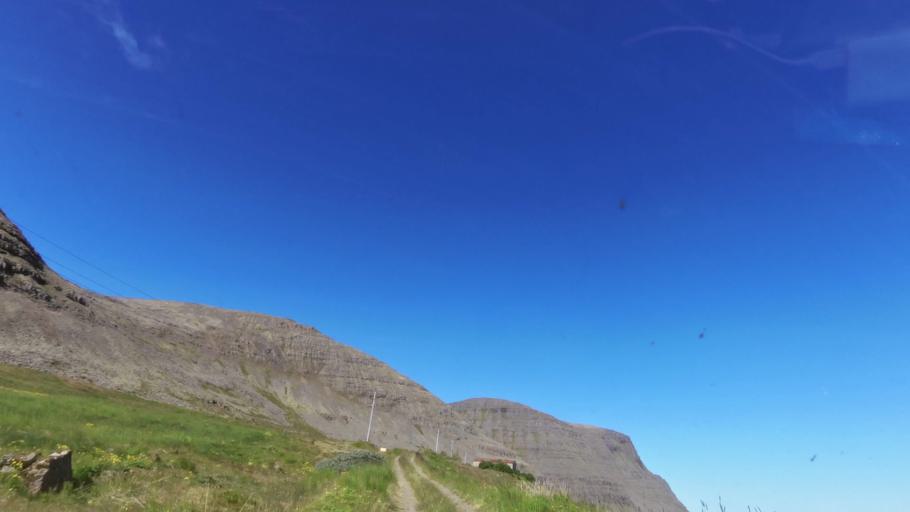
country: IS
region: West
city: Olafsvik
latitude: 65.6223
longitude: -23.8715
